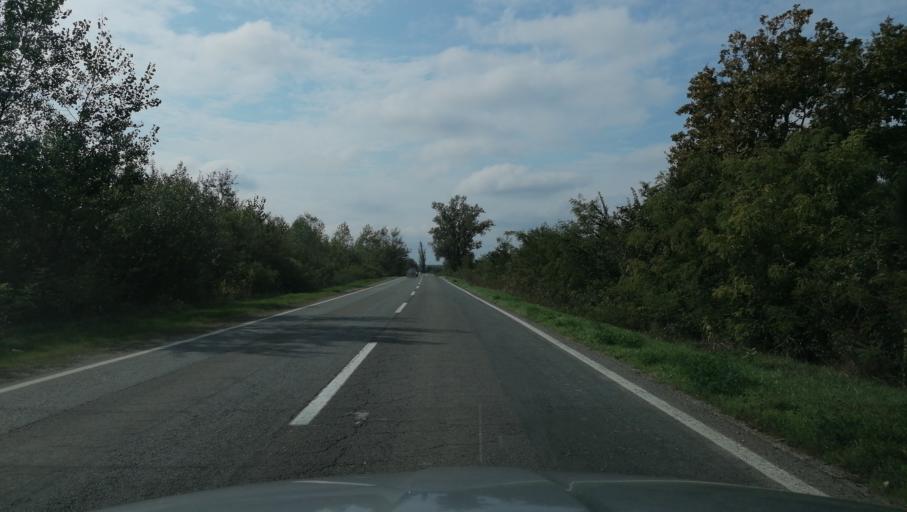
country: RS
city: Bosut
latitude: 44.9233
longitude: 19.3212
